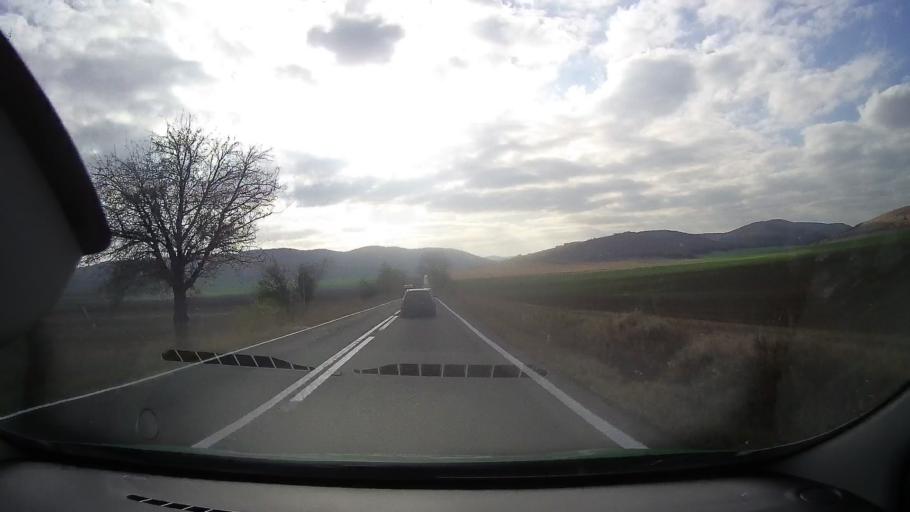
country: RO
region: Tulcea
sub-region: Comuna Nalbant
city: Nicolae Balcescu
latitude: 44.9793
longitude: 28.5479
